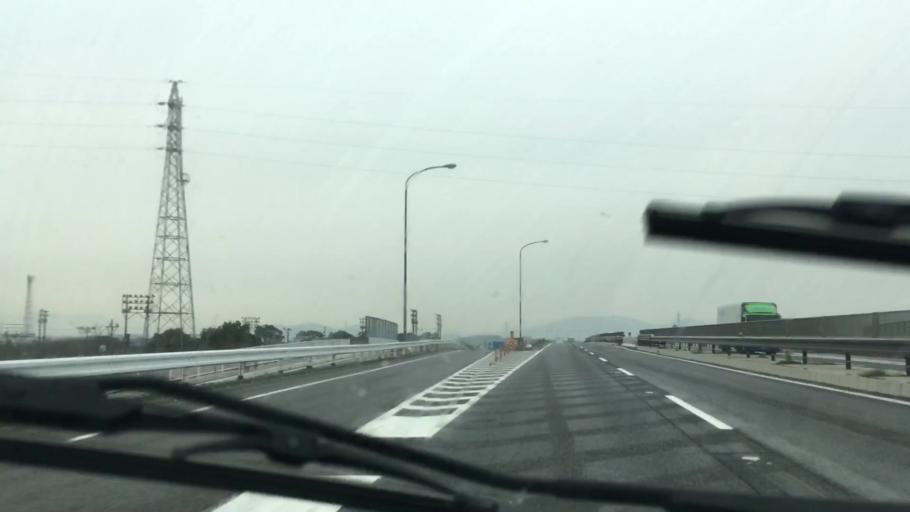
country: JP
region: Aichi
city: Nishio
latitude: 34.9008
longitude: 137.0693
